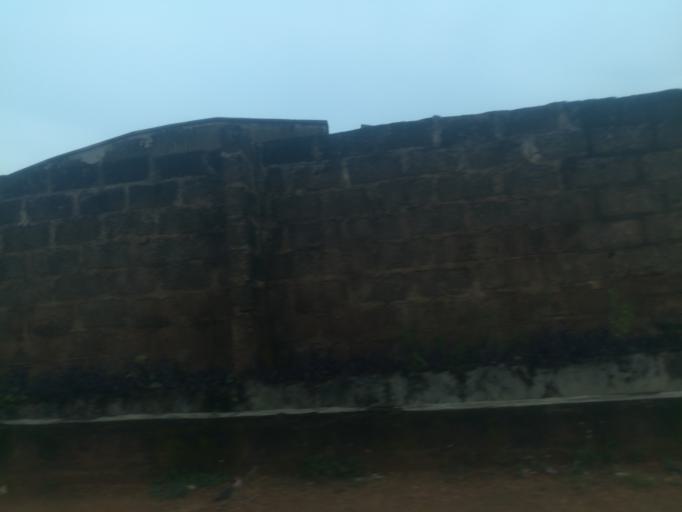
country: NG
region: Oyo
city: Ibadan
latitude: 7.3537
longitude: 3.8274
